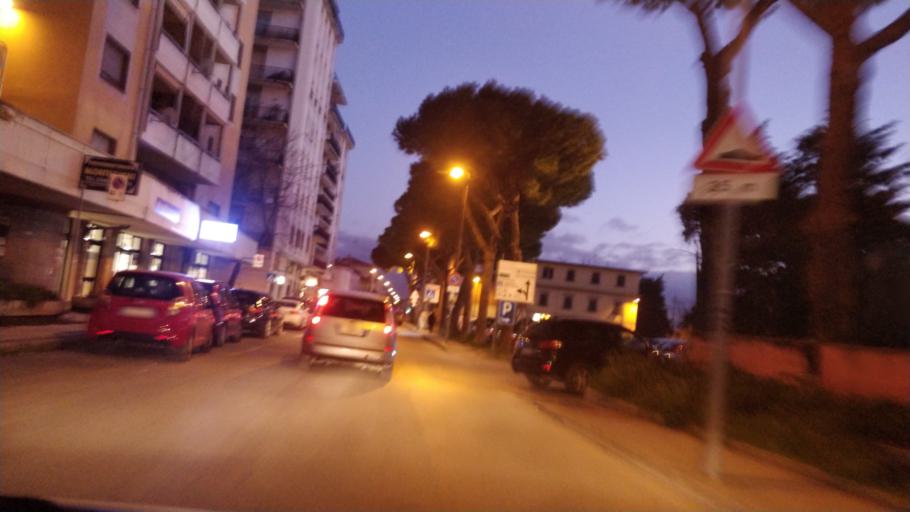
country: IT
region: Tuscany
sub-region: Provincia di Livorno
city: Cecina
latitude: 43.3090
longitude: 10.5159
